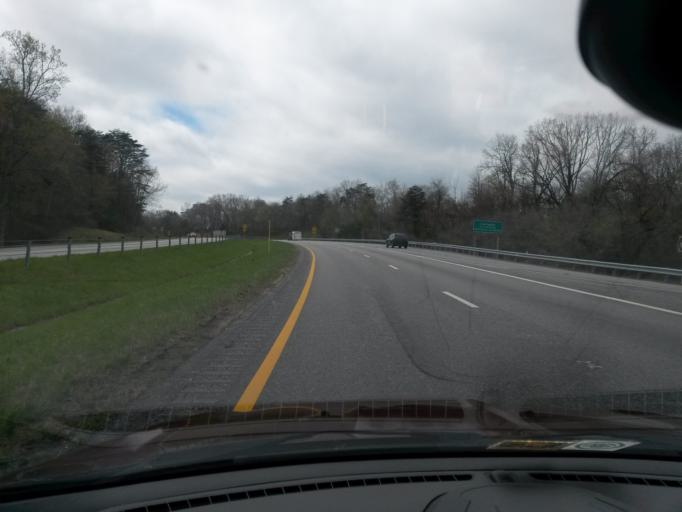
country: US
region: Virginia
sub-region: City of Covington
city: Fairlawn
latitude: 37.7767
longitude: -79.9761
